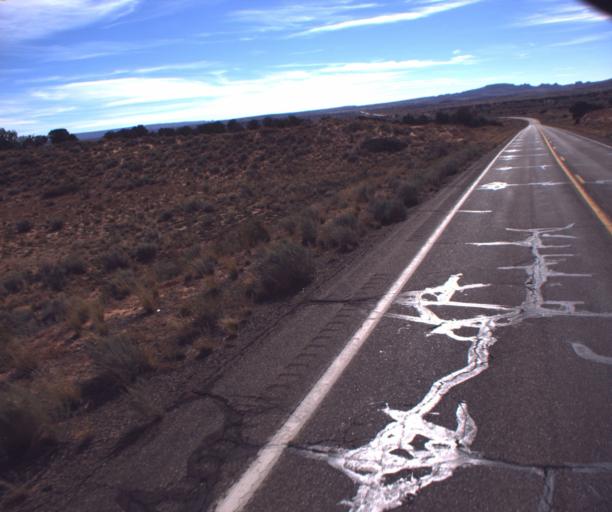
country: US
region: Arizona
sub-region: Coconino County
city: Kaibito
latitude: 36.6279
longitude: -111.2048
